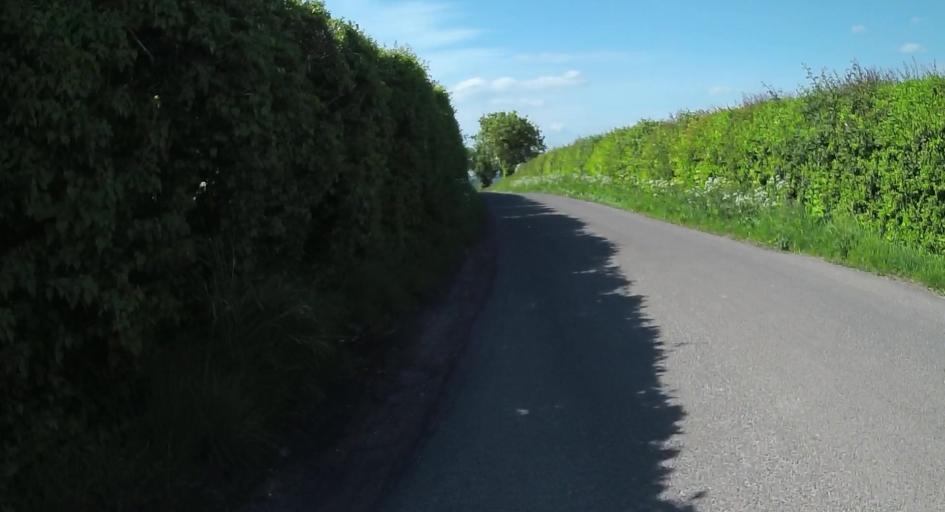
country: GB
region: England
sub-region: Hampshire
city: Kings Worthy
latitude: 51.0686
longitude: -1.2729
